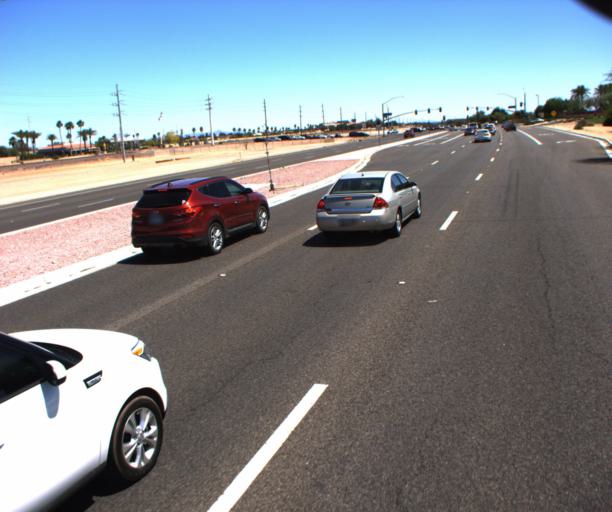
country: US
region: Arizona
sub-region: Maricopa County
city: Sun City West
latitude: 33.6708
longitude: -112.3923
